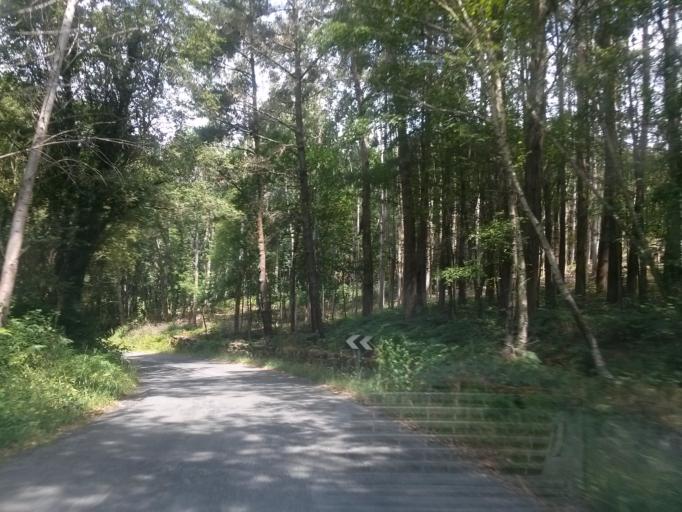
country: ES
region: Galicia
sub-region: Provincia de Lugo
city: Outeiro de Rei
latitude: 43.0445
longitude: -7.6149
